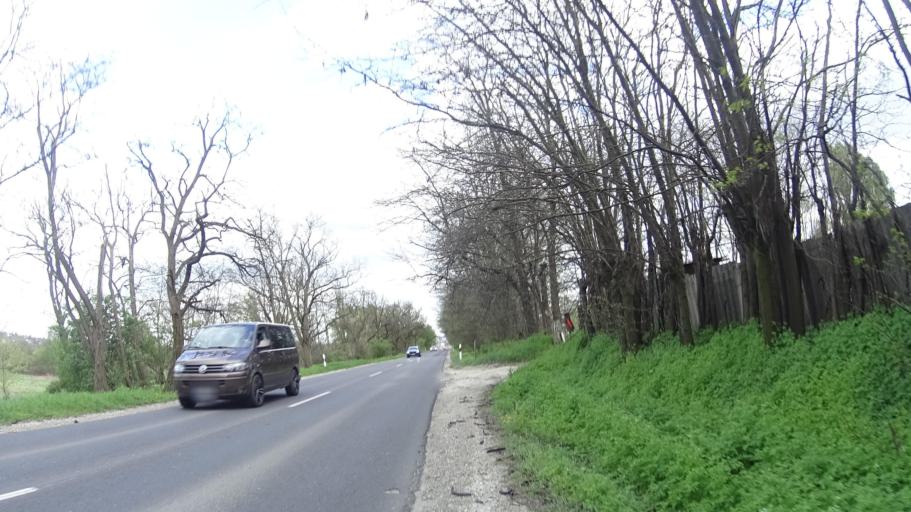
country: HU
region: Pest
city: Szada
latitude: 47.6204
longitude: 19.3271
